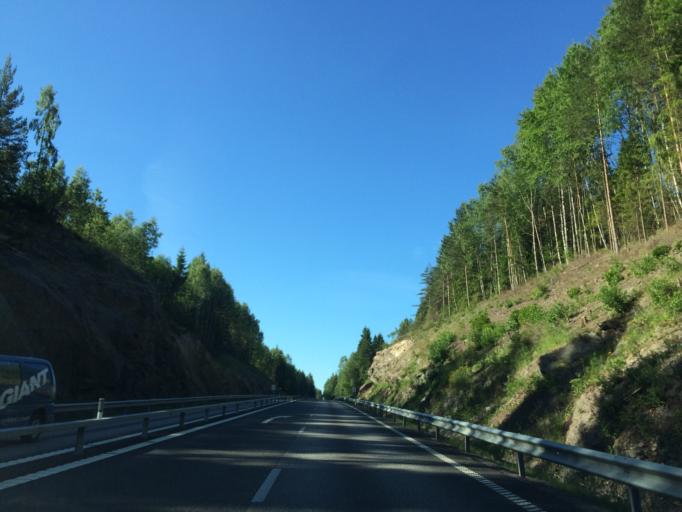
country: SE
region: OEstergoetland
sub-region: Motala Kommun
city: Ryd
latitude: 58.7684
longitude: 14.9934
